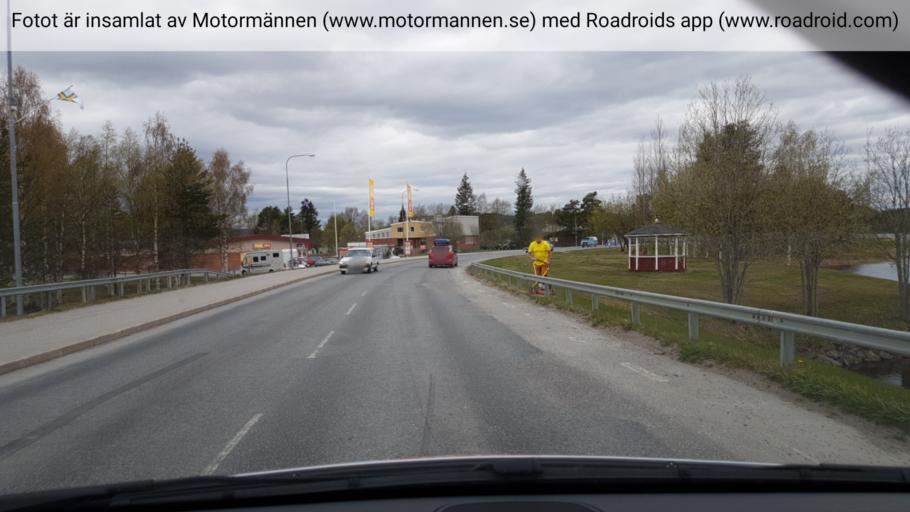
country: SE
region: Vaesterbotten
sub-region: Sorsele Kommun
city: Sorsele
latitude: 65.5353
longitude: 17.5344
